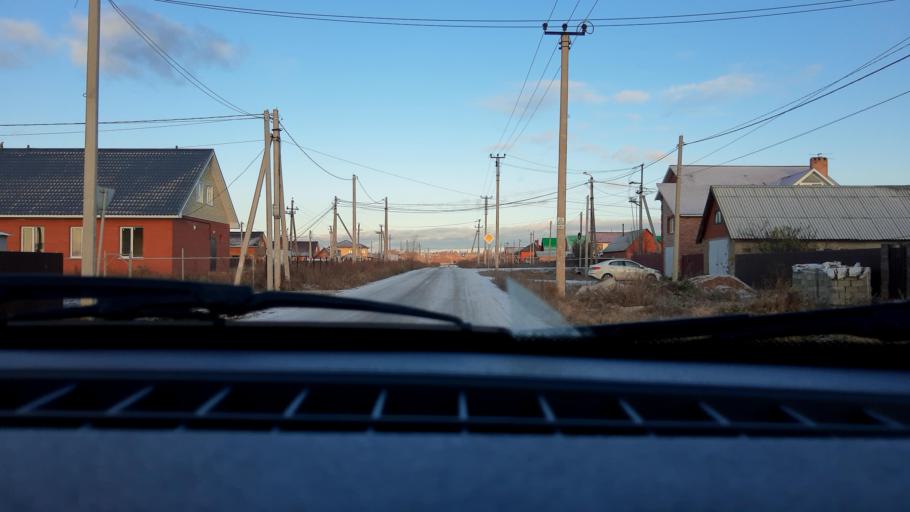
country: RU
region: Bashkortostan
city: Mikhaylovka
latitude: 54.7889
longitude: 55.8262
